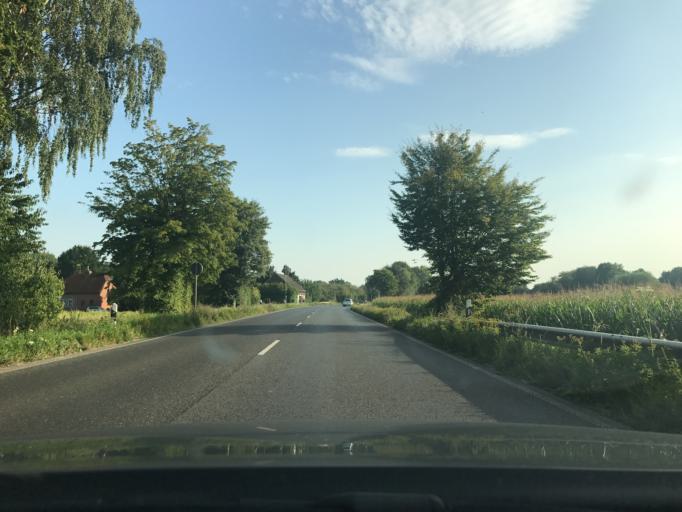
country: DE
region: North Rhine-Westphalia
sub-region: Regierungsbezirk Dusseldorf
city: Rheurdt
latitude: 51.4006
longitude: 6.4983
